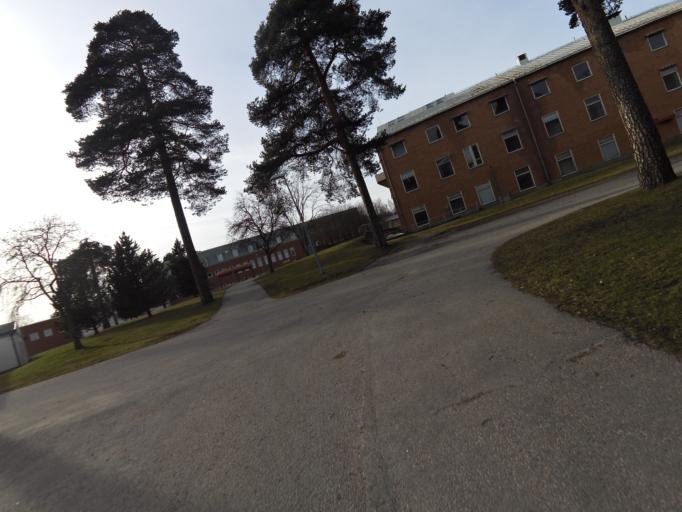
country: SE
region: Gaevleborg
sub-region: Gavle Kommun
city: Gavle
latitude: 60.6764
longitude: 17.1174
